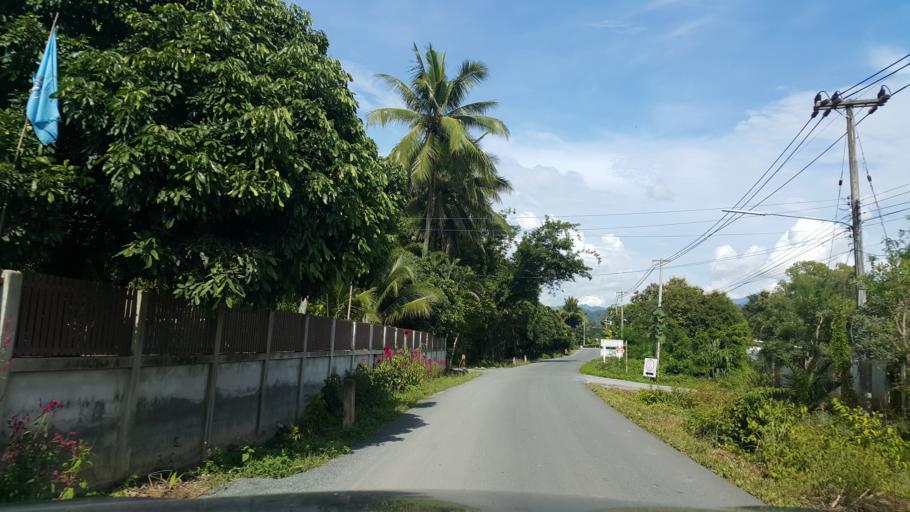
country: TH
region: Chiang Mai
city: Mae On
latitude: 18.8335
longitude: 99.1998
